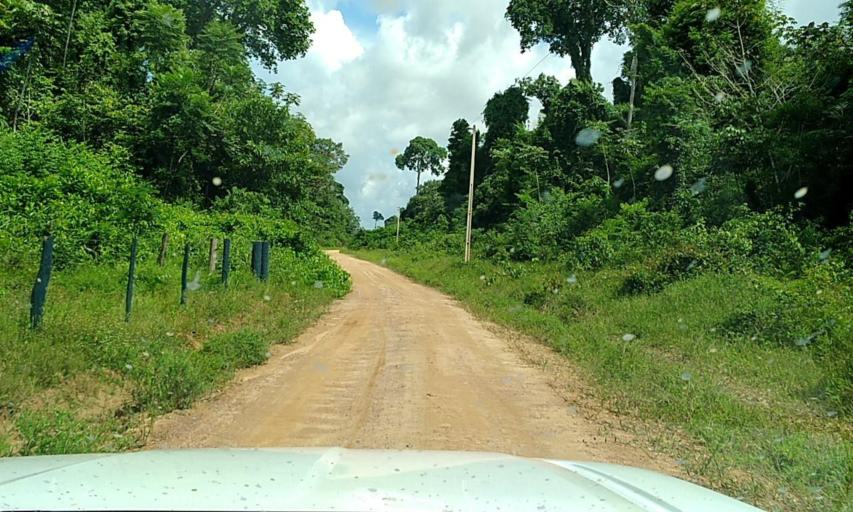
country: BR
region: Para
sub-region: Senador Jose Porfirio
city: Senador Jose Porfirio
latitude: -2.5219
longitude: -51.8334
